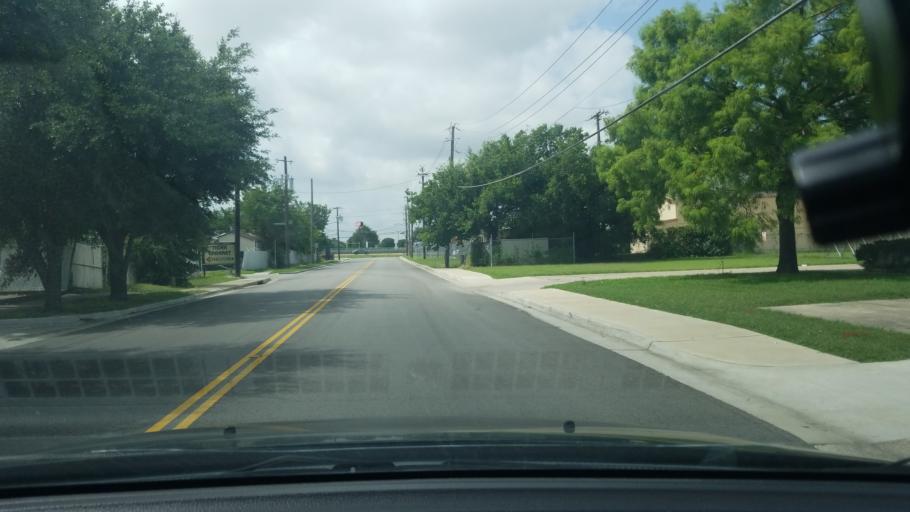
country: US
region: Texas
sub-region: Dallas County
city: Mesquite
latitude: 32.7986
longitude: -96.6882
